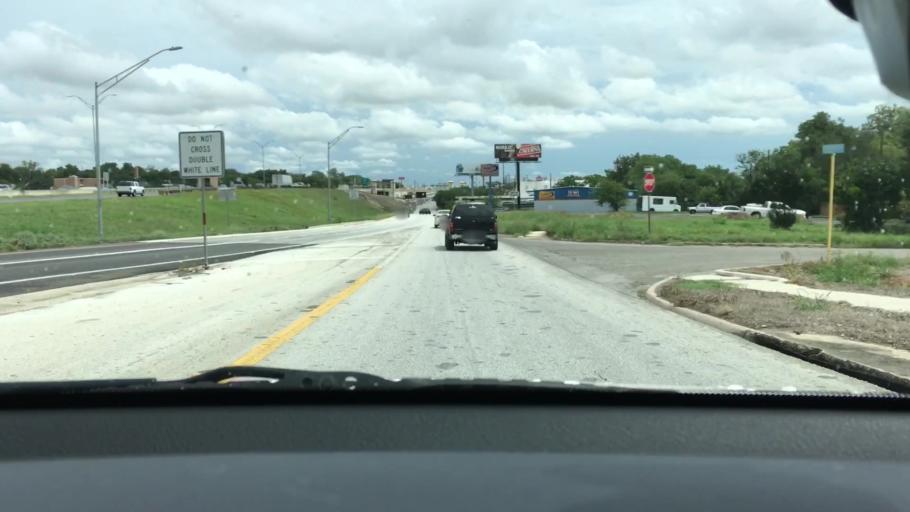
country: US
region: Texas
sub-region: Bexar County
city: Terrell Hills
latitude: 29.4381
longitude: -98.4583
